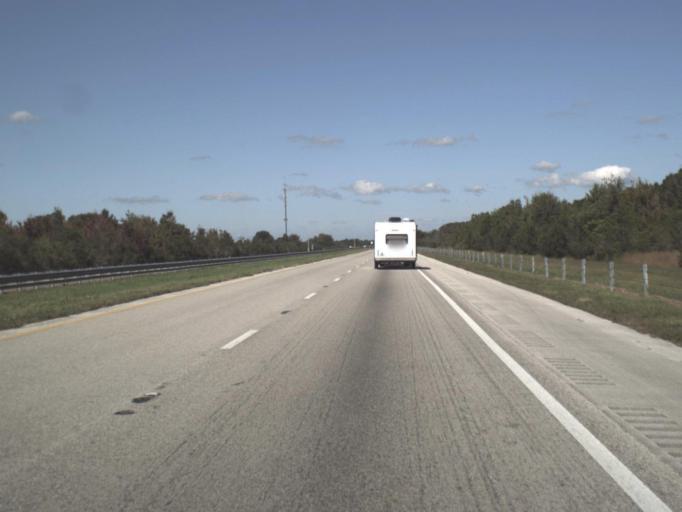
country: US
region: Florida
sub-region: Osceola County
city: Saint Cloud
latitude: 28.0186
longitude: -81.1775
